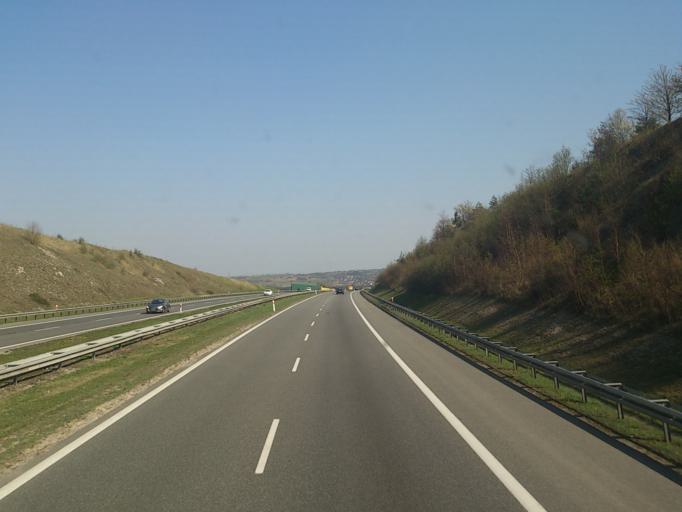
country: PL
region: Lesser Poland Voivodeship
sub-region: Powiat chrzanowski
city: Grojec
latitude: 50.0978
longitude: 19.5590
